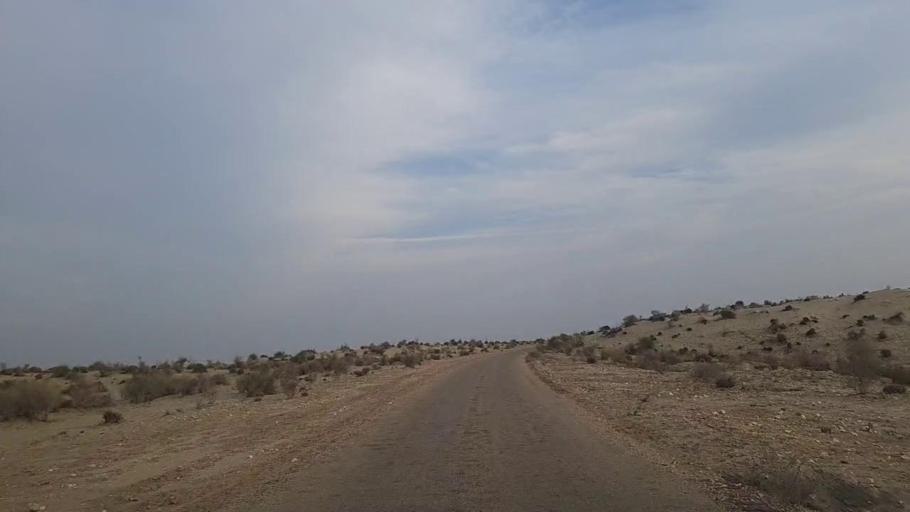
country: PK
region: Sindh
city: Daur
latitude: 26.5043
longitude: 68.5175
